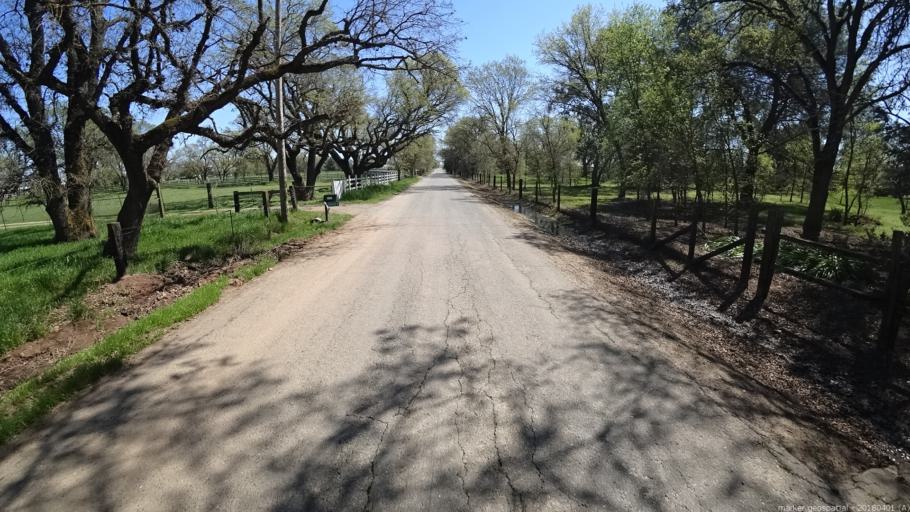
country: US
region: California
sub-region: Sacramento County
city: Rancho Murieta
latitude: 38.4487
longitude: -121.1675
